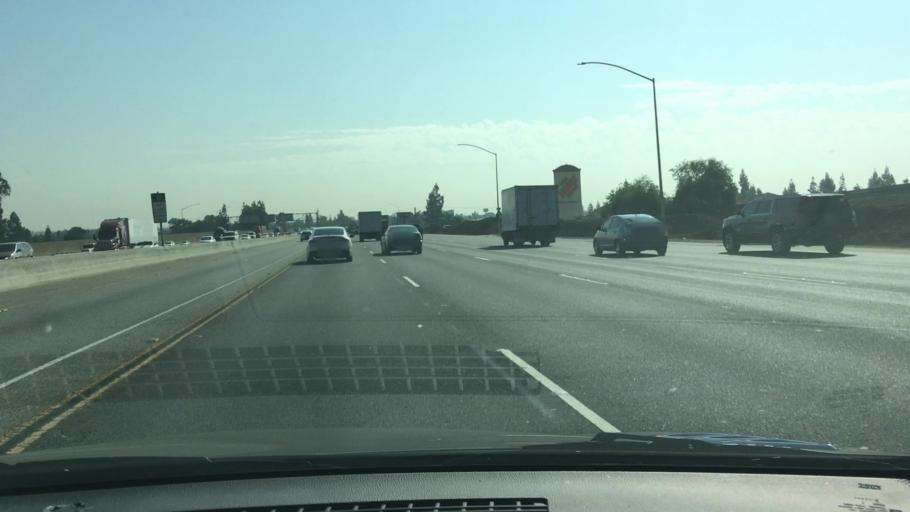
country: US
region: California
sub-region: Los Angeles County
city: Pomona
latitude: 34.0237
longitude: -117.7448
